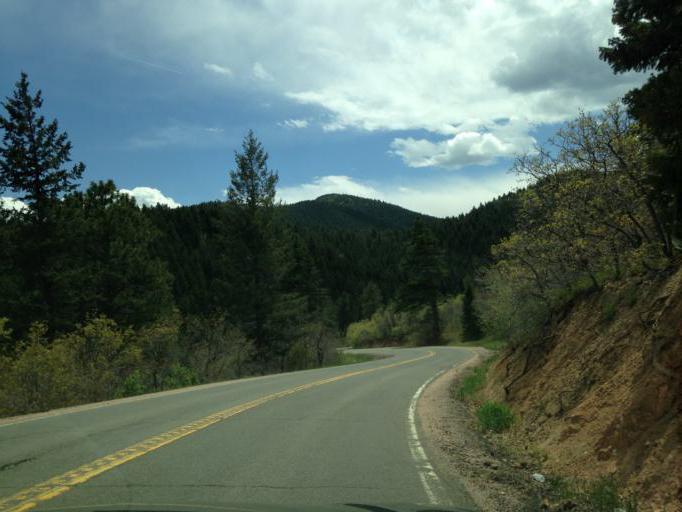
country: US
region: Colorado
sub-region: Jefferson County
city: Ken Caryl
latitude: 39.5075
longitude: -105.1874
